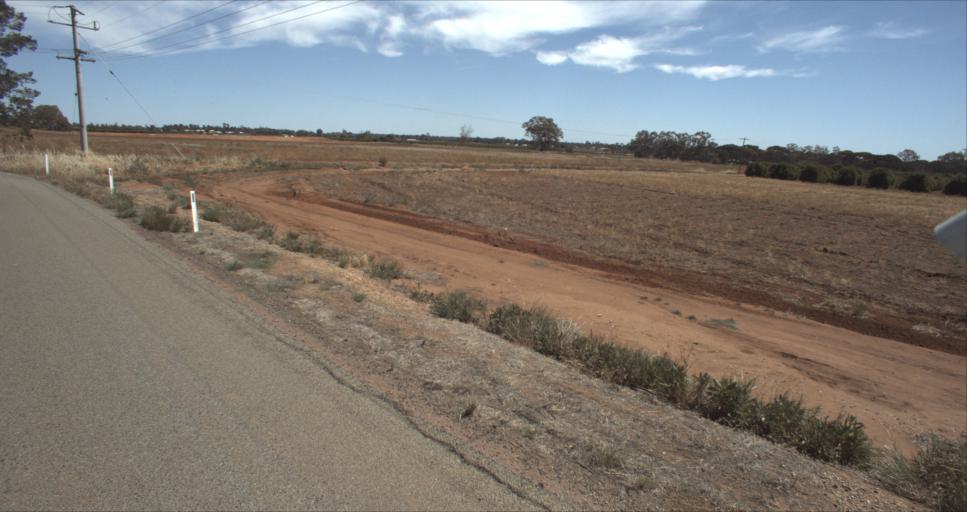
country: AU
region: New South Wales
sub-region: Leeton
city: Leeton
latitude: -34.6053
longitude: 146.4335
